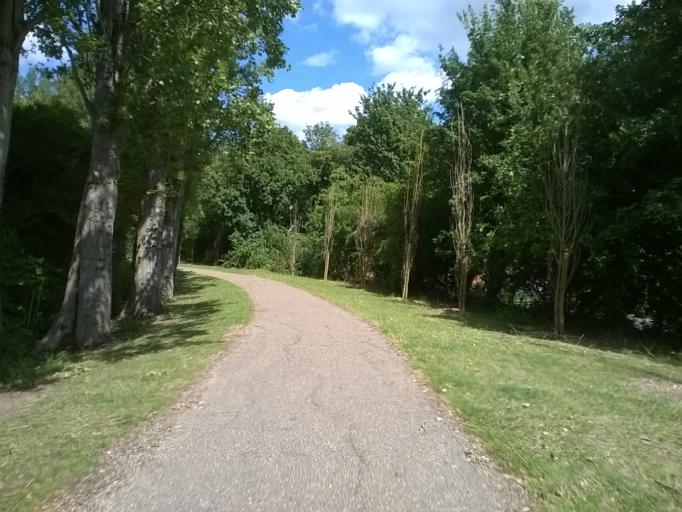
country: GB
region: England
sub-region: Milton Keynes
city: Milton Keynes
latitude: 52.0674
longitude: -0.7447
